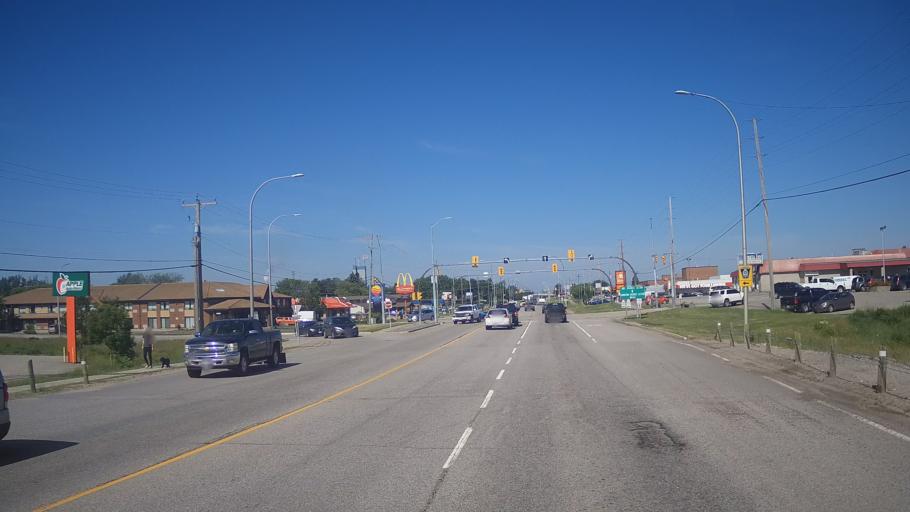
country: CA
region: Ontario
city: Dryden
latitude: 49.7862
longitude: -92.8200
